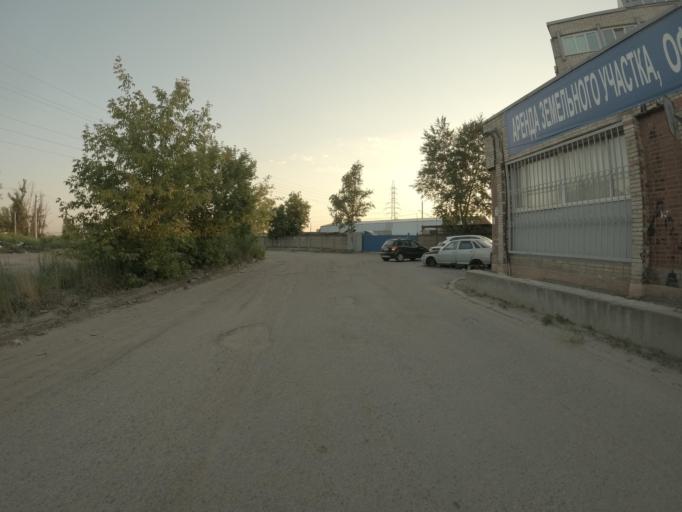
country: RU
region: St.-Petersburg
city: Avtovo
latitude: 59.8796
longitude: 30.2858
